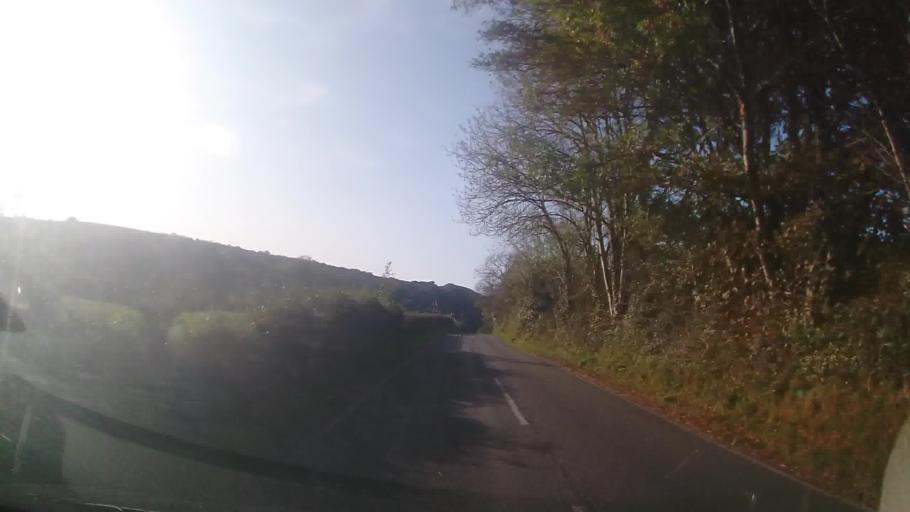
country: GB
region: Wales
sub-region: Pembrokeshire
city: Fishguard
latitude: 51.9793
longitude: -4.9295
